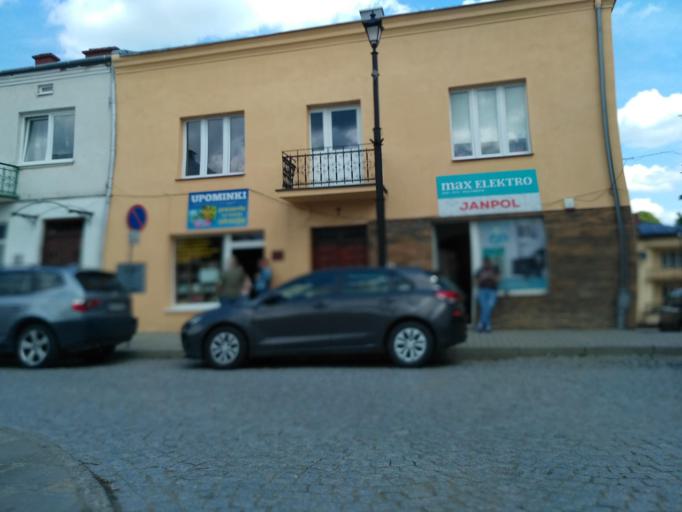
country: PL
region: Subcarpathian Voivodeship
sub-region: Powiat krosnienski
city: Dukla
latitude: 49.5552
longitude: 21.6849
